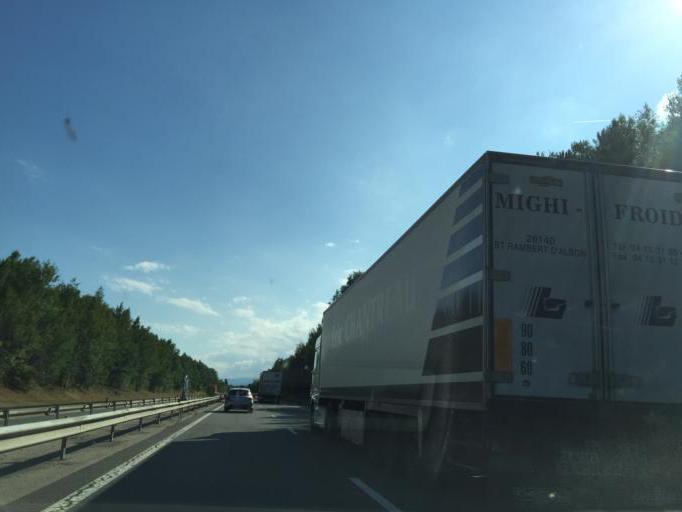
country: FR
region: Rhone-Alpes
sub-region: Departement de la Loire
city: Feurs
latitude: 45.7137
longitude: 4.1710
